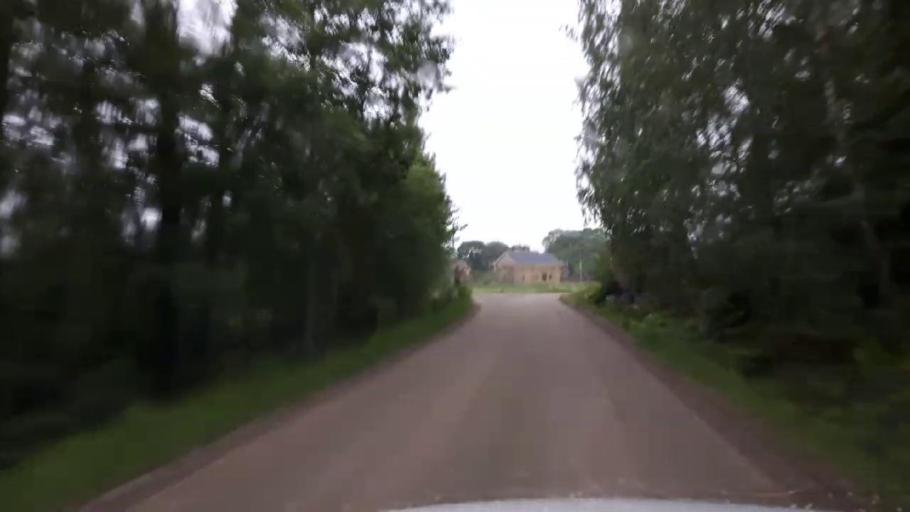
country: SE
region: Soedermanland
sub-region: Eskilstuna Kommun
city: Kvicksund
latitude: 59.4115
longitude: 16.2454
